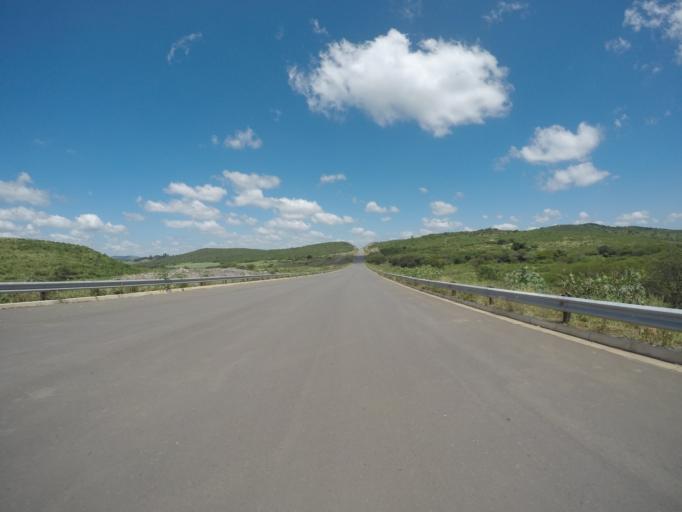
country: ZA
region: KwaZulu-Natal
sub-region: uThungulu District Municipality
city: Empangeni
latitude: -28.6168
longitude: 31.7552
